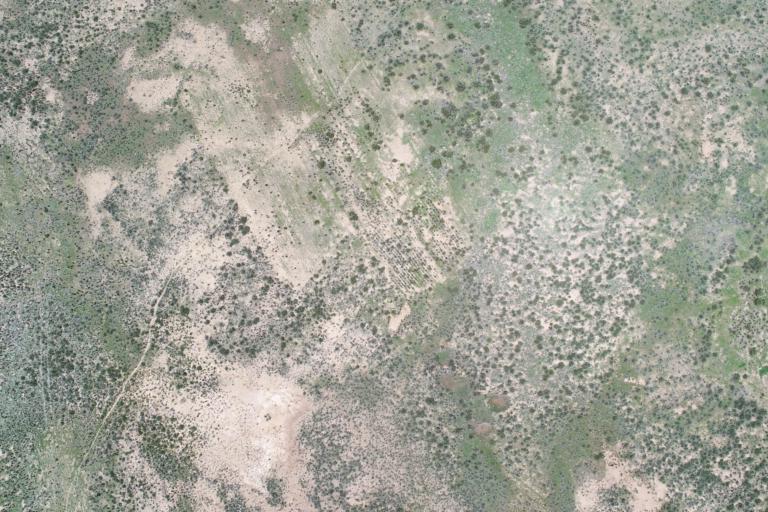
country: BO
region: La Paz
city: Curahuara de Carangas
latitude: -17.3258
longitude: -68.5092
